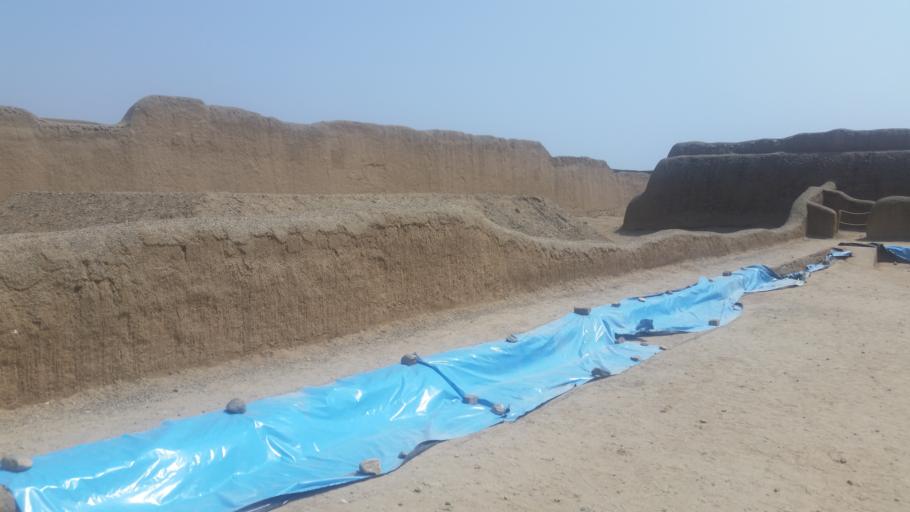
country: PE
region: La Libertad
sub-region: Provincia de Trujillo
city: Buenos Aires
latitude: -8.1118
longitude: -79.0742
